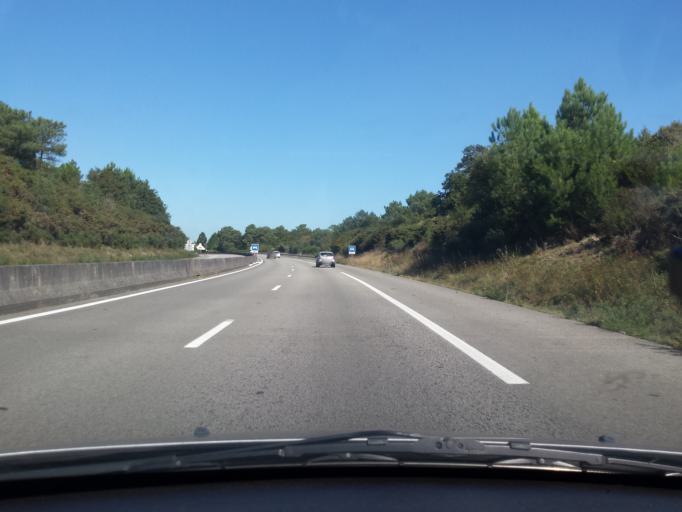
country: FR
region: Brittany
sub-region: Departement du Morbihan
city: Saint-Ave
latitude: 47.6936
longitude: -2.7650
